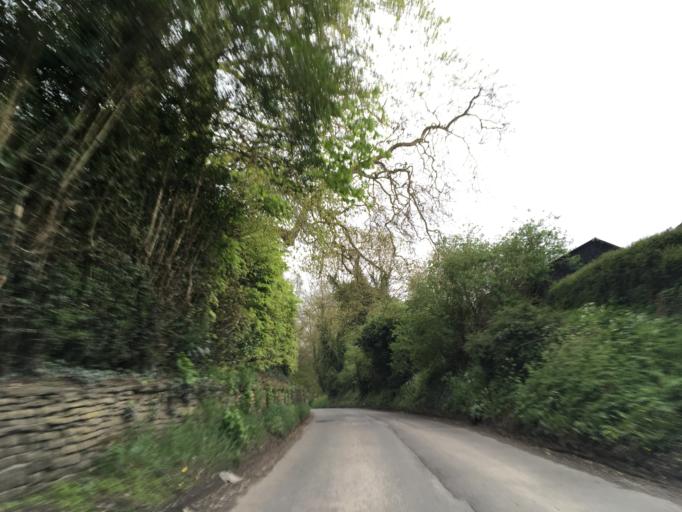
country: GB
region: England
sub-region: Gloucestershire
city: Wotton-under-Edge
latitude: 51.6246
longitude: -2.3403
